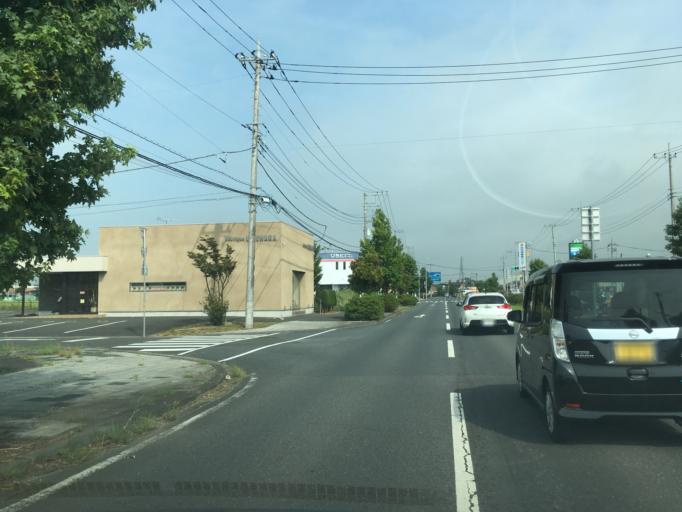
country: JP
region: Ibaraki
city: Oarai
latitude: 36.3468
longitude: 140.5821
